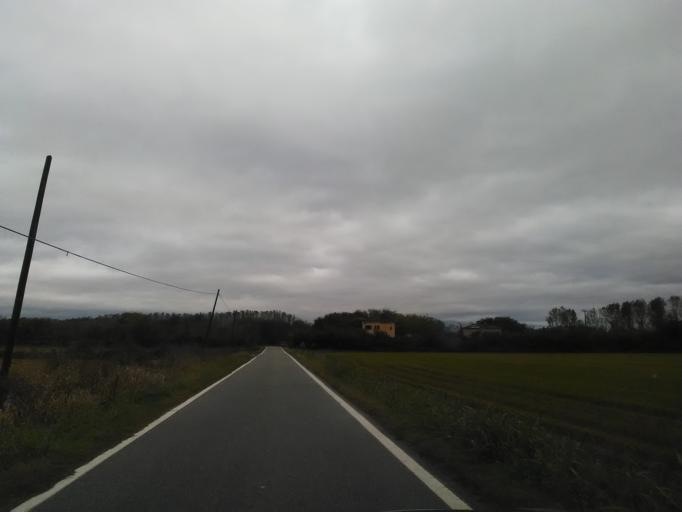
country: IT
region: Piedmont
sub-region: Provincia di Vercelli
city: Carisio
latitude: 45.3994
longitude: 8.2438
